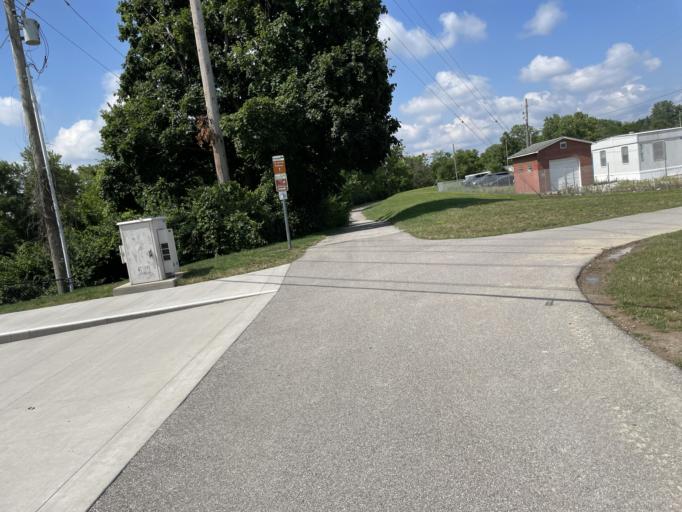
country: US
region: Indiana
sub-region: Allen County
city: Fort Wayne
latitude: 41.0831
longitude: -85.1444
